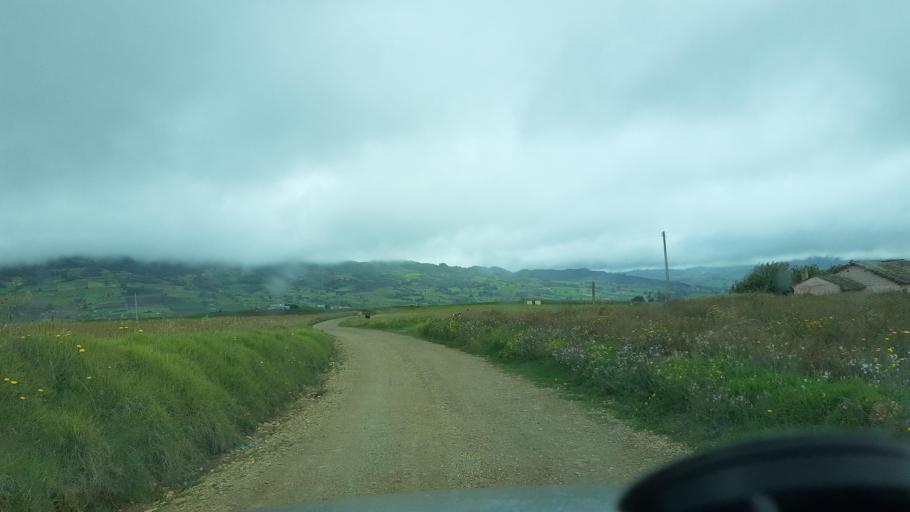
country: CO
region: Boyaca
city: Cucaita
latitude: 5.5209
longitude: -73.4381
